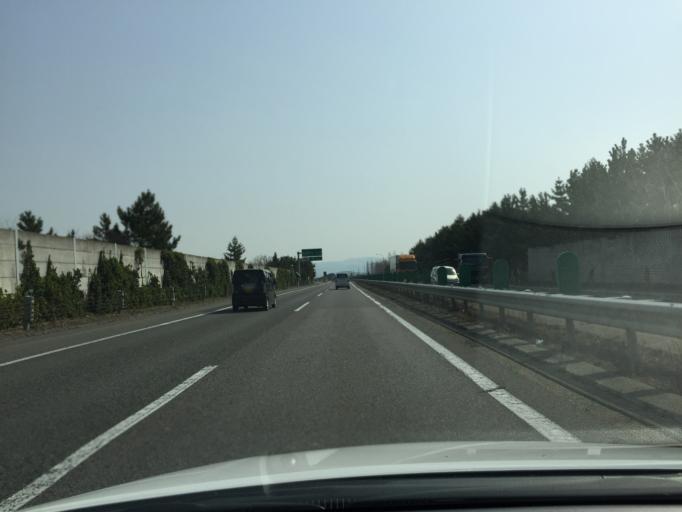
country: JP
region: Fukushima
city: Fukushima-shi
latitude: 37.8020
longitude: 140.4494
